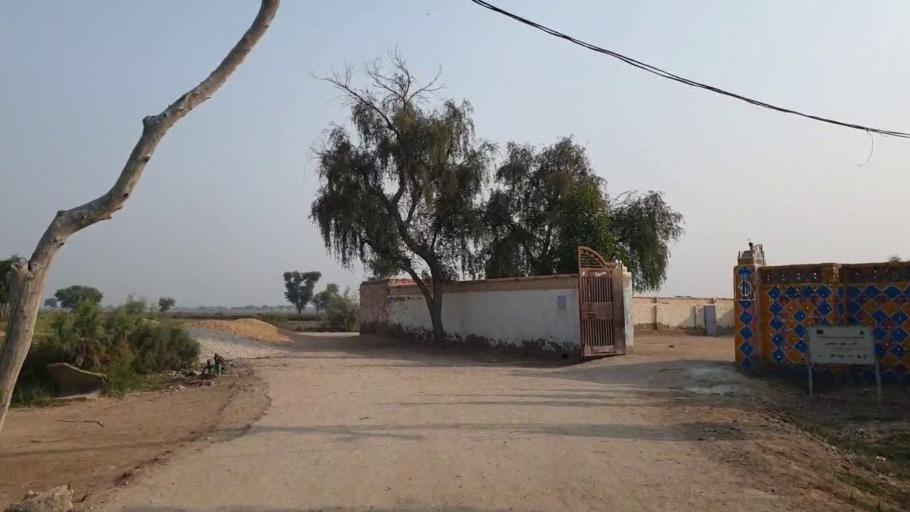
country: PK
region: Sindh
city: Bhan
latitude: 26.4735
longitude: 67.7263
